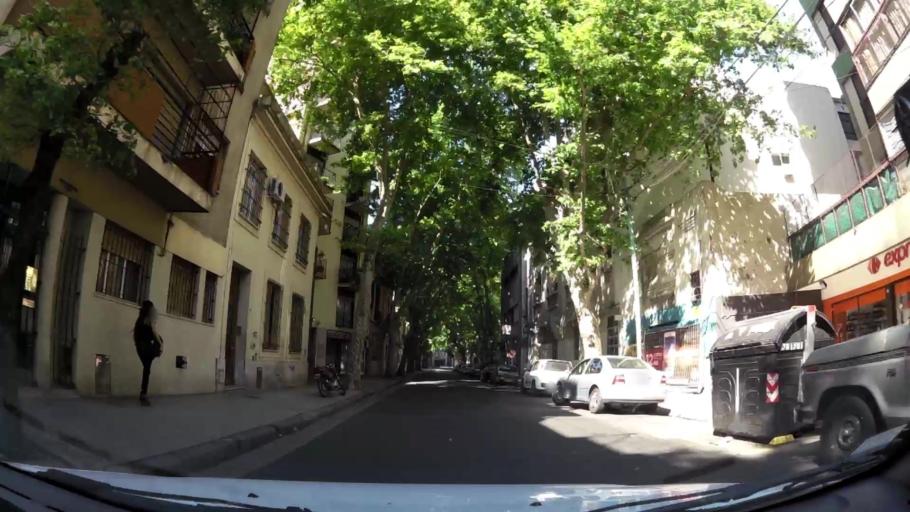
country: AR
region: Buenos Aires F.D.
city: Buenos Aires
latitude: -34.6124
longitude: -58.4129
